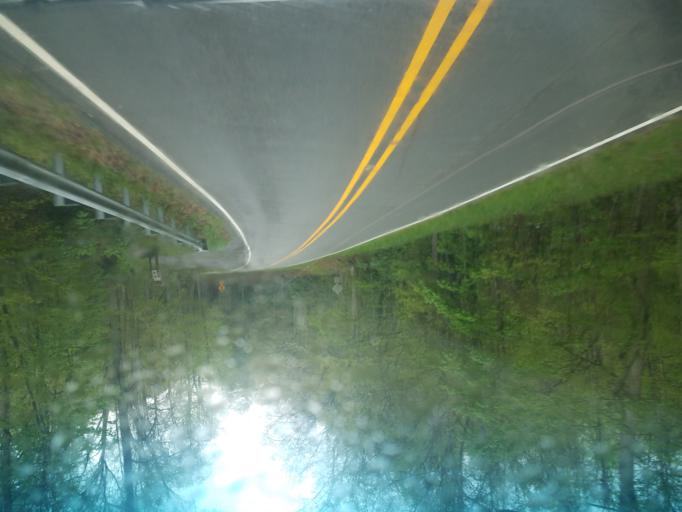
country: US
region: Virginia
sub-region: Washington County
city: Glade Spring
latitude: 36.6444
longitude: -81.7414
